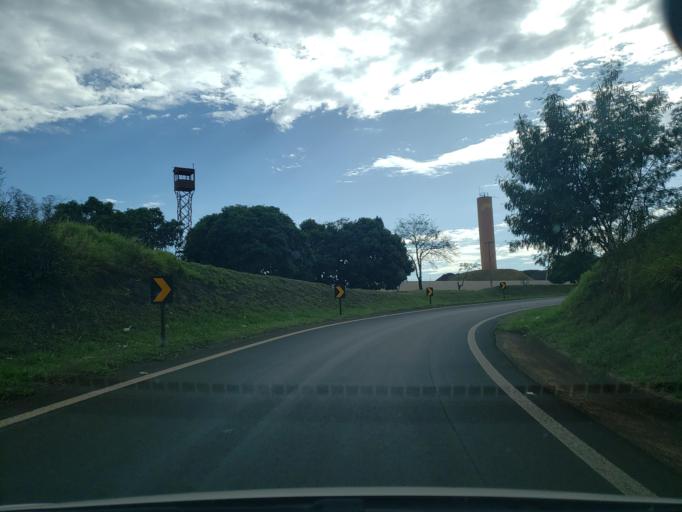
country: BR
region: Sao Paulo
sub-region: Jau
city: Jau
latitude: -22.2560
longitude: -48.5518
